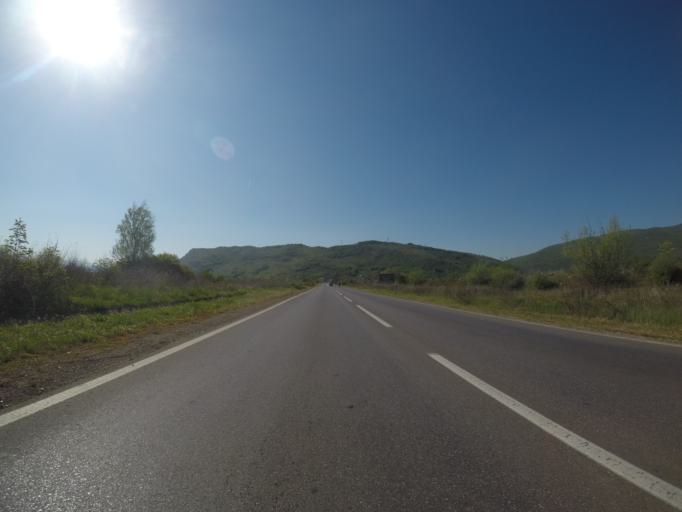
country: ME
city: Spuz
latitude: 42.4677
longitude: 19.1746
